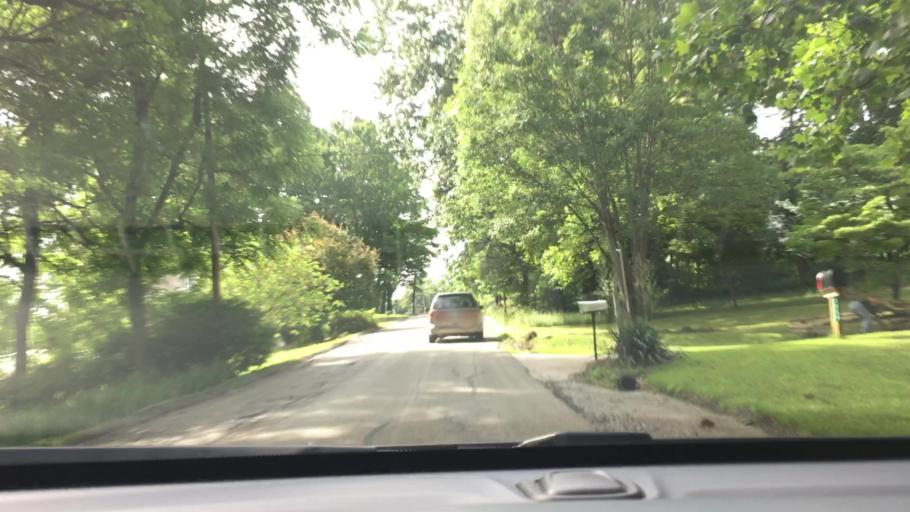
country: US
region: Pennsylvania
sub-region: Westmoreland County
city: New Stanton
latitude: 40.2606
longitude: -79.6181
